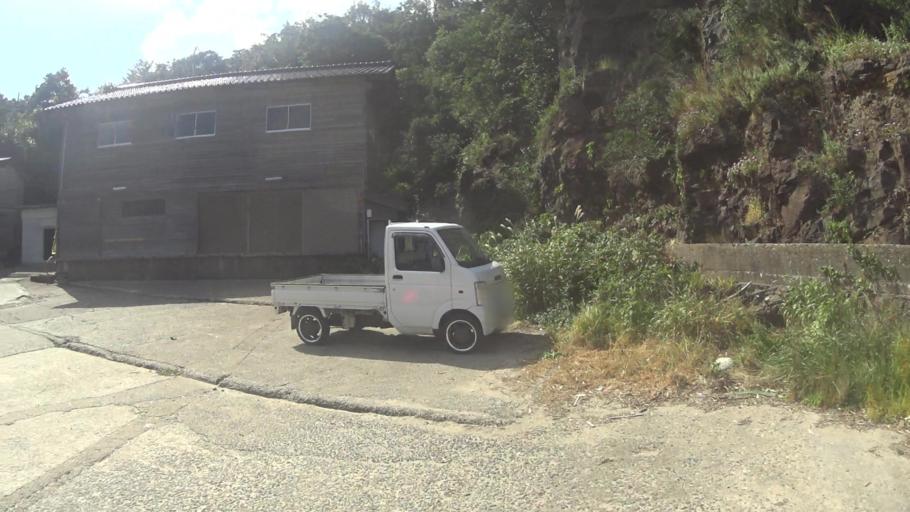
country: JP
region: Kyoto
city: Miyazu
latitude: 35.7333
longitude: 135.2733
